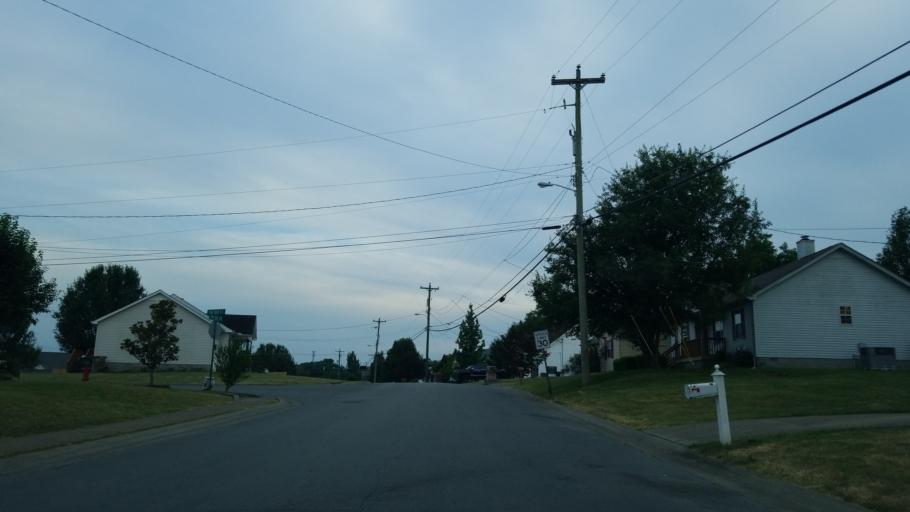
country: US
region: Tennessee
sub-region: Rutherford County
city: La Vergne
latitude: 36.0471
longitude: -86.5901
